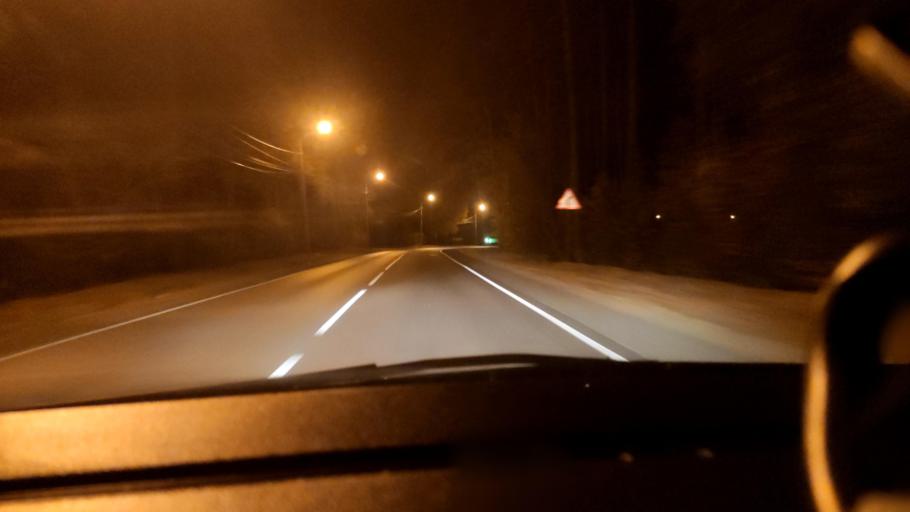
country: RU
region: Voronezj
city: Pridonskoy
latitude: 51.6270
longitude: 39.0819
